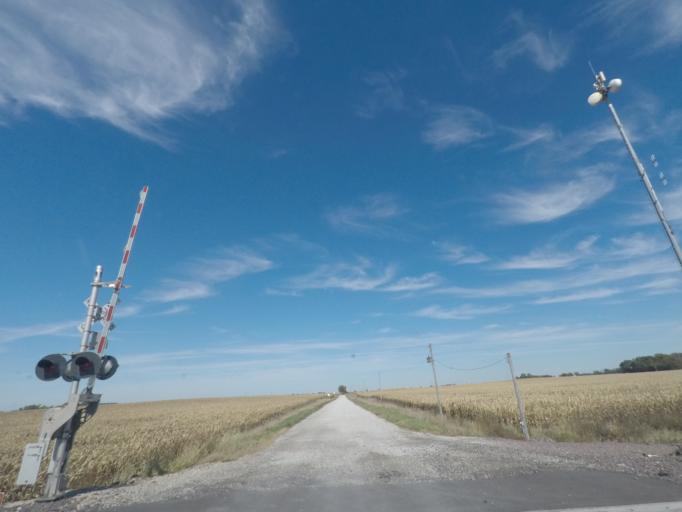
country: US
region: Iowa
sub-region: Story County
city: Nevada
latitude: 42.0191
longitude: -93.3573
